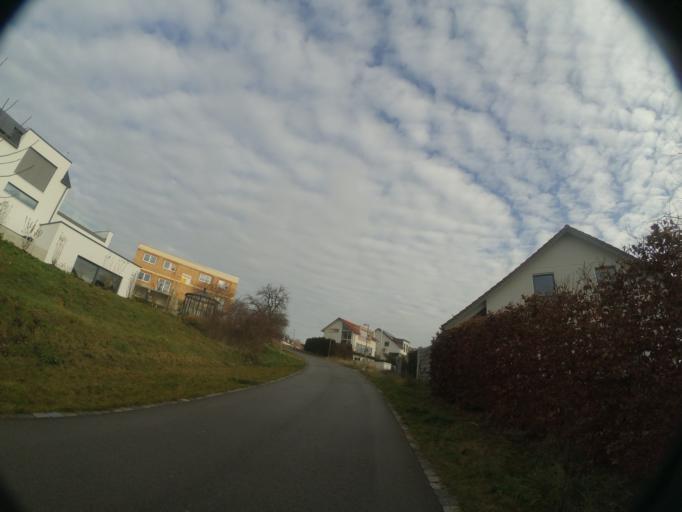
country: DE
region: Baden-Wuerttemberg
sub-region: Tuebingen Region
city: Ulm
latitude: 48.3772
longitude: 9.9493
